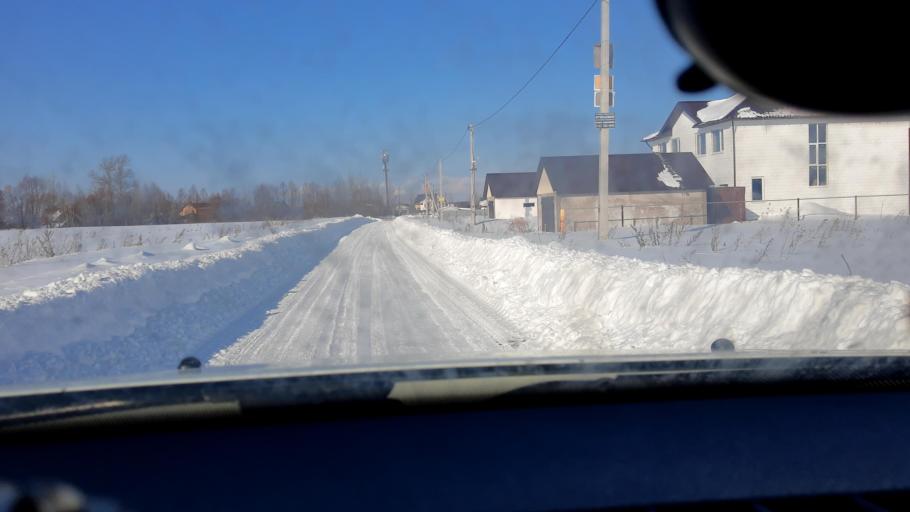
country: RU
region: Bashkortostan
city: Ufa
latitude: 54.7039
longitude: 56.1056
